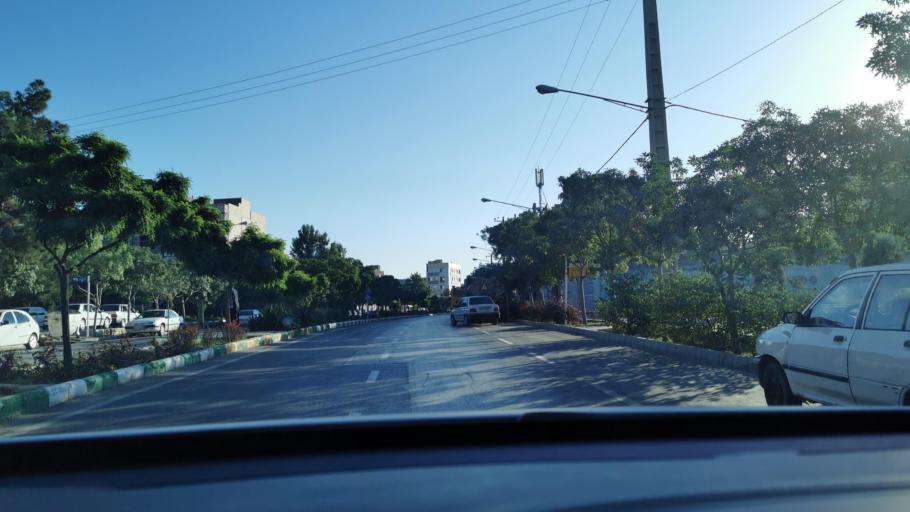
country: IR
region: Razavi Khorasan
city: Mashhad
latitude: 36.3482
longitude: 59.4775
